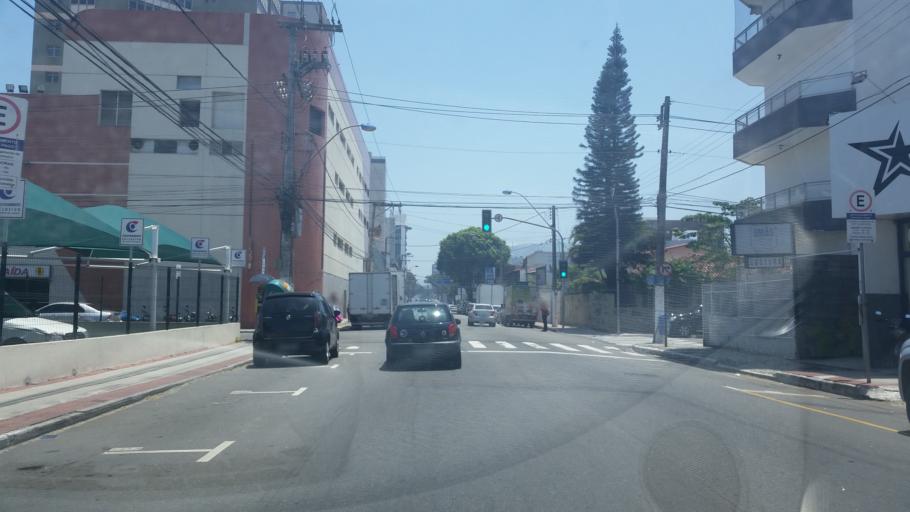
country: BR
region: Espirito Santo
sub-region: Vila Velha
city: Vila Velha
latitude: -20.3357
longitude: -40.2878
